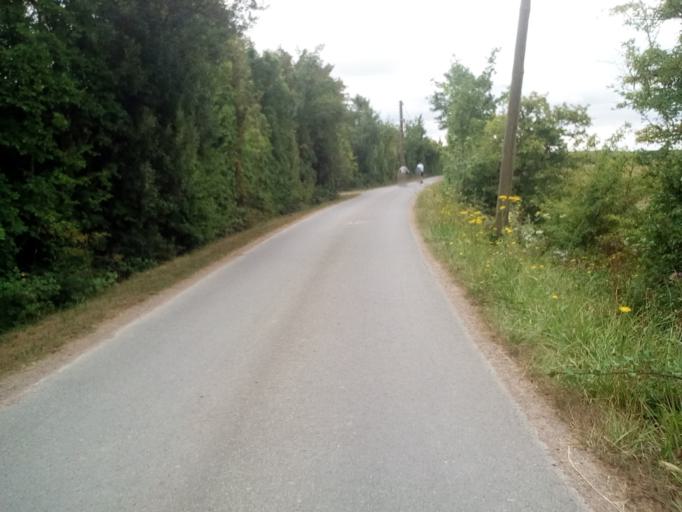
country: FR
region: Lower Normandy
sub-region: Departement du Calvados
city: Cabourg
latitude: 49.2583
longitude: -0.1328
